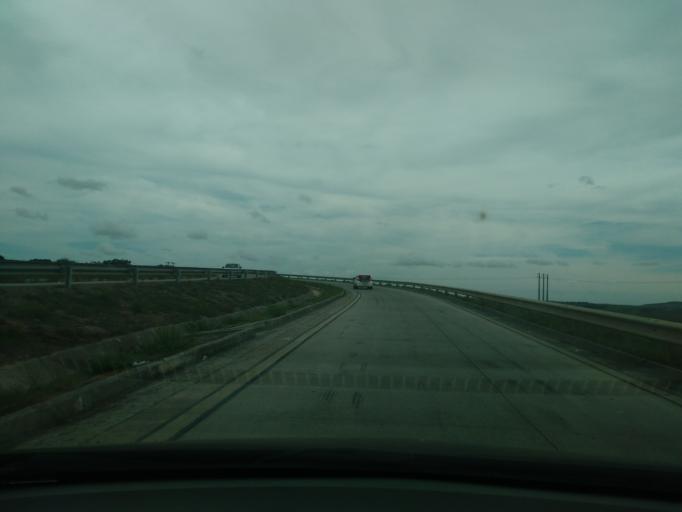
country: BR
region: Alagoas
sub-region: Rio Largo
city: Rio Largo
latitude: -9.4396
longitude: -35.8378
